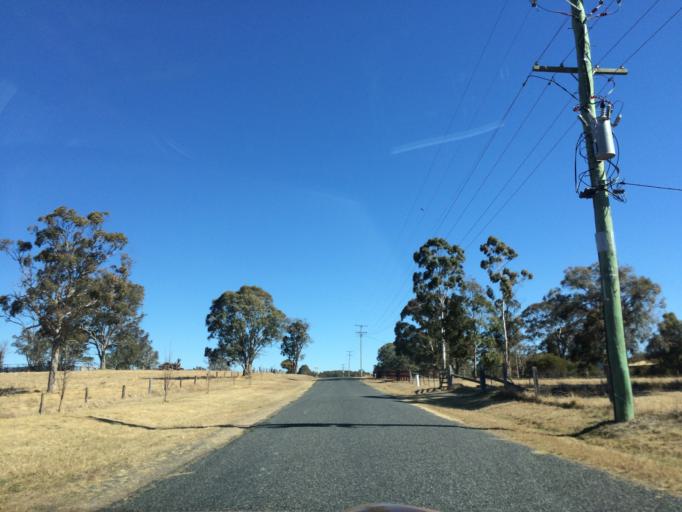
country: AU
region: Queensland
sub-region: Southern Downs
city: Stanthorpe
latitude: -28.6379
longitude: 152.0881
